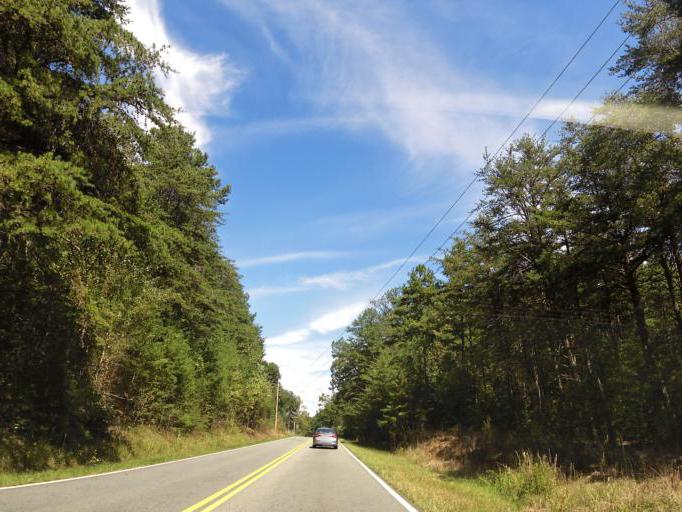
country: US
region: Georgia
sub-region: Pickens County
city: Nelson
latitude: 34.4297
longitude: -84.2755
